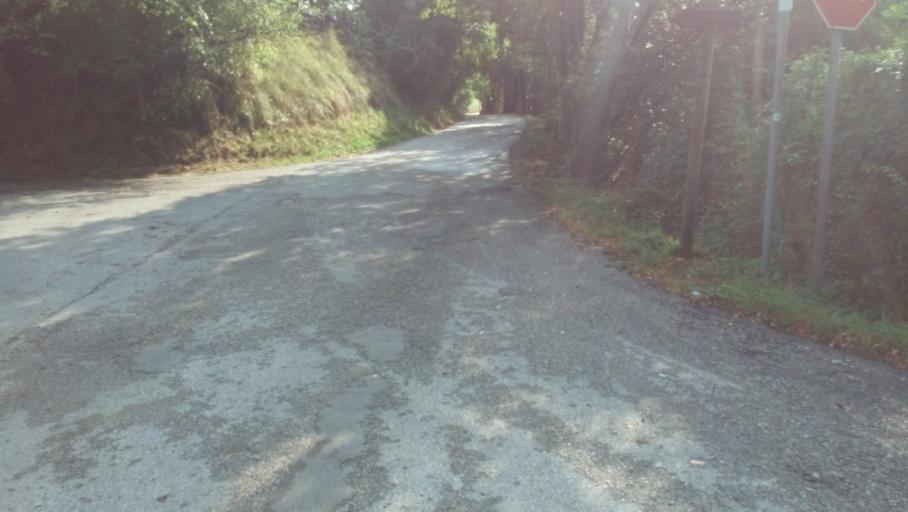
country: IT
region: Veneto
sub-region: Provincia di Vicenza
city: Creazzo
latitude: 45.5393
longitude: 11.4611
